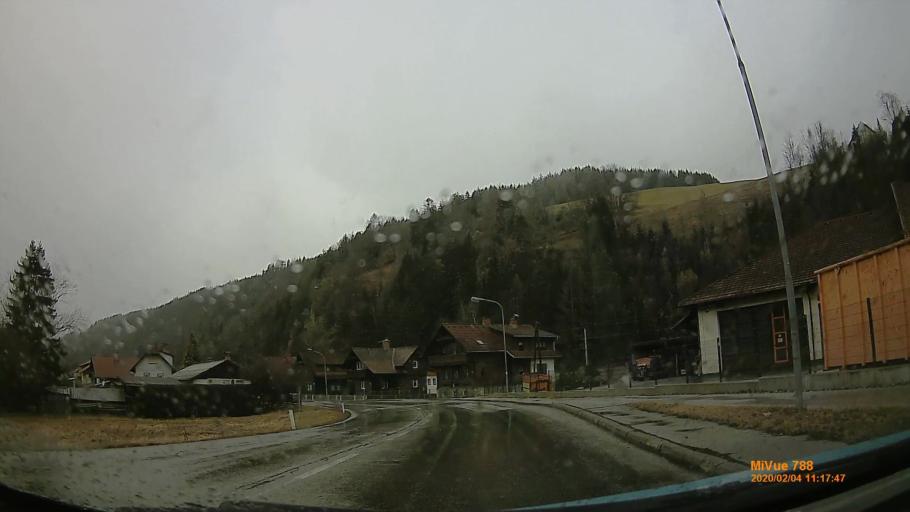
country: AT
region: Styria
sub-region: Politischer Bezirk Bruck-Muerzzuschlag
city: Muerzzuschlag
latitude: 47.6049
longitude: 15.6994
